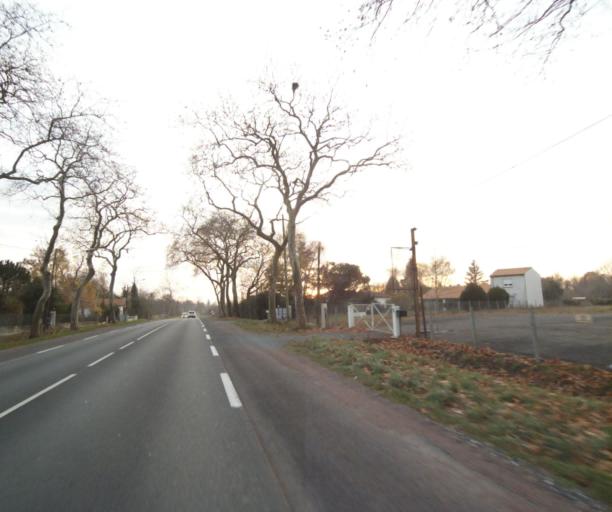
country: FR
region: Poitou-Charentes
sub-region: Departement de la Charente-Maritime
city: Fontcouverte
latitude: 45.7606
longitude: -0.5885
